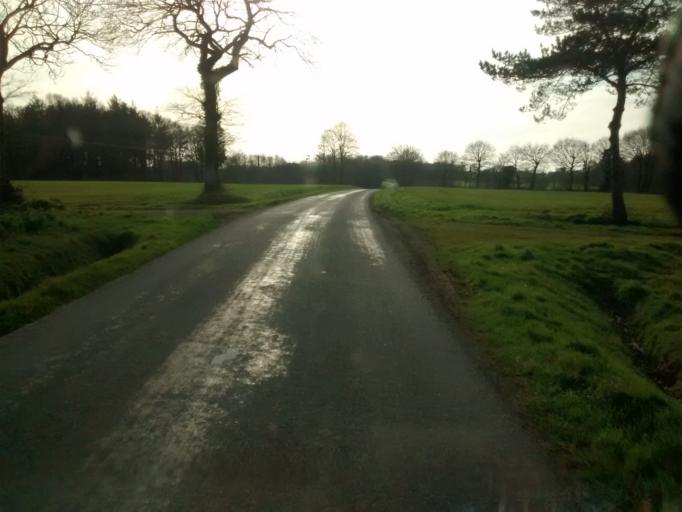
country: FR
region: Brittany
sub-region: Departement du Morbihan
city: Mauron
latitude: 48.1520
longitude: -2.3191
